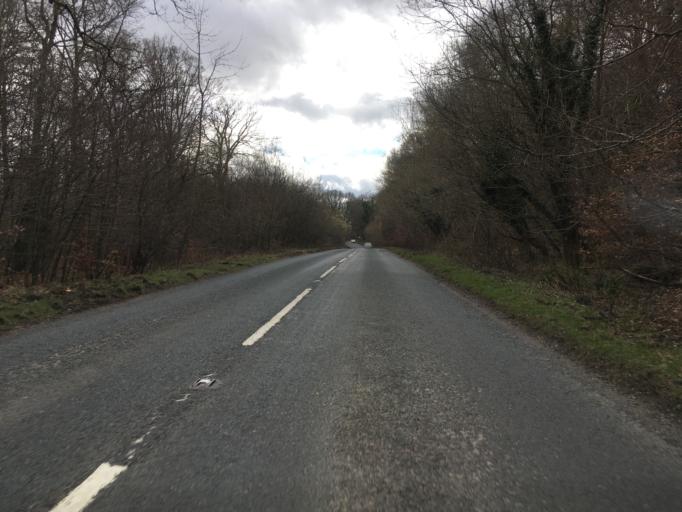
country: GB
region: England
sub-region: Gloucestershire
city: Coleford
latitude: 51.8079
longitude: -2.5969
